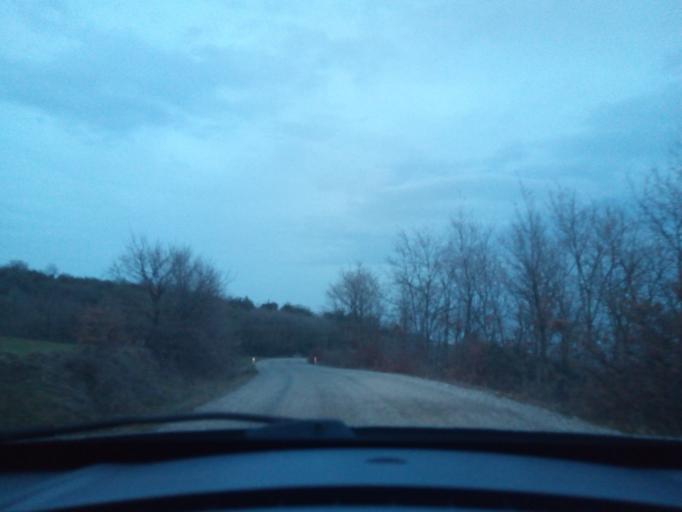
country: TR
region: Balikesir
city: Omerkoy
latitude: 39.9137
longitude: 28.0495
